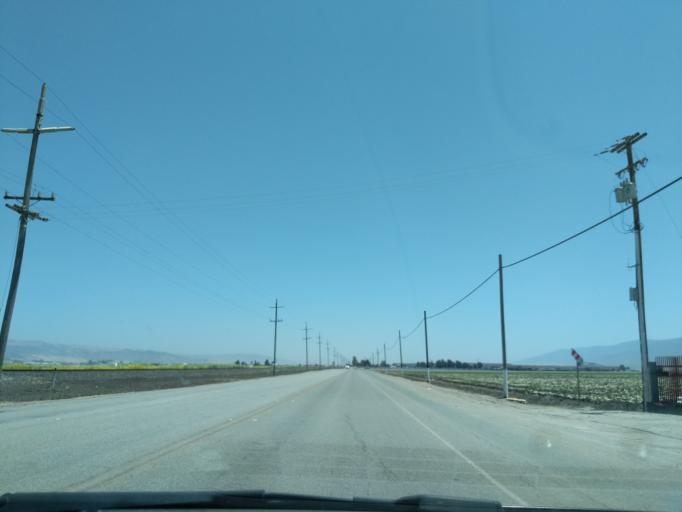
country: US
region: California
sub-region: Monterey County
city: Salinas
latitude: 36.6369
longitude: -121.6013
